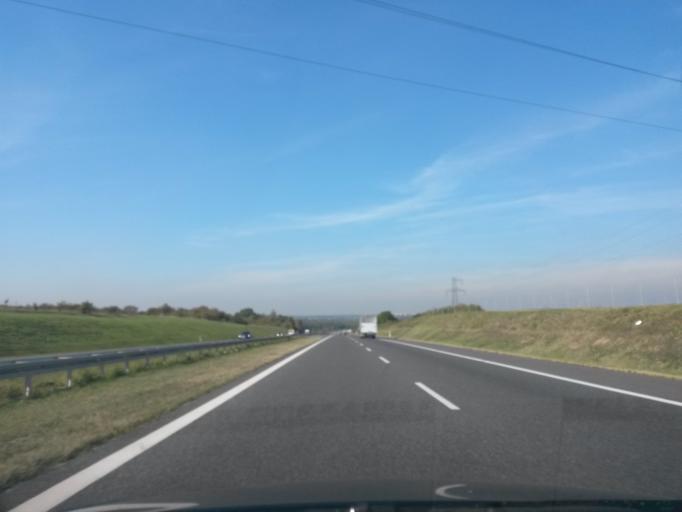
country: PL
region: Silesian Voivodeship
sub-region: Powiat bierunsko-ledzinski
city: Imielin
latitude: 50.1743
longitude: 19.2069
